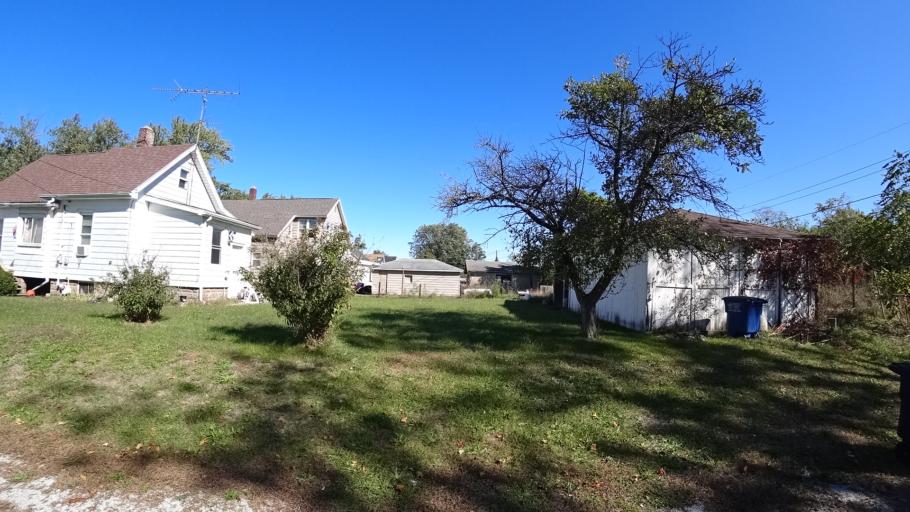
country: US
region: Indiana
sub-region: LaPorte County
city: Michigan City
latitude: 41.7033
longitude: -86.9118
